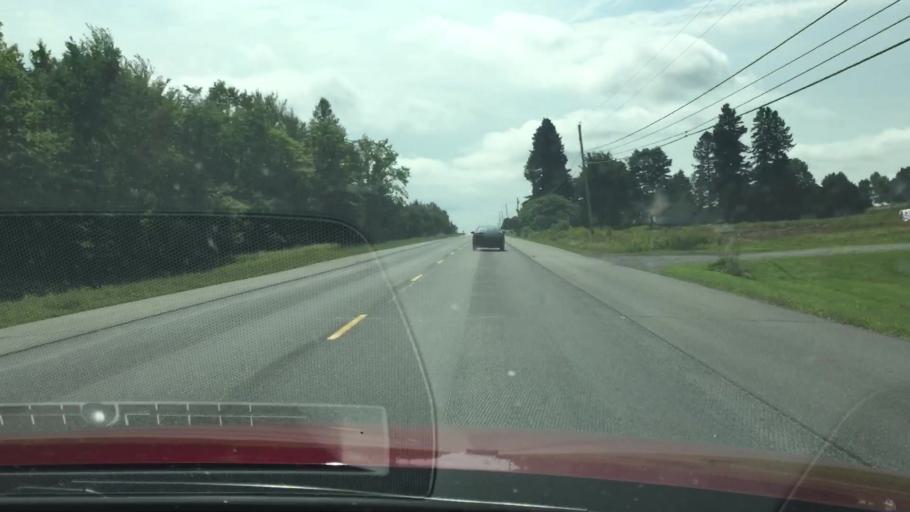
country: US
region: Maine
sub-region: Aroostook County
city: Houlton
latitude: 46.3456
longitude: -67.8420
